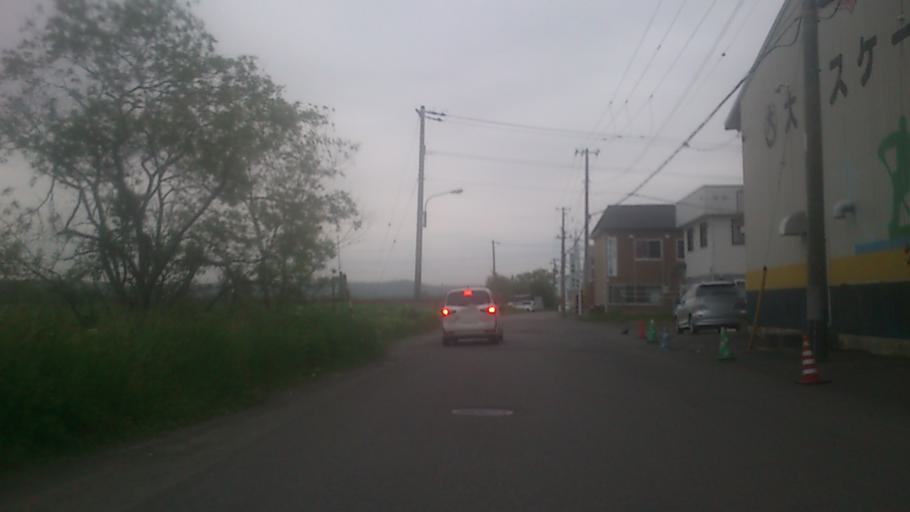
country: JP
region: Hokkaido
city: Kushiro
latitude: 42.9990
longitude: 144.4176
